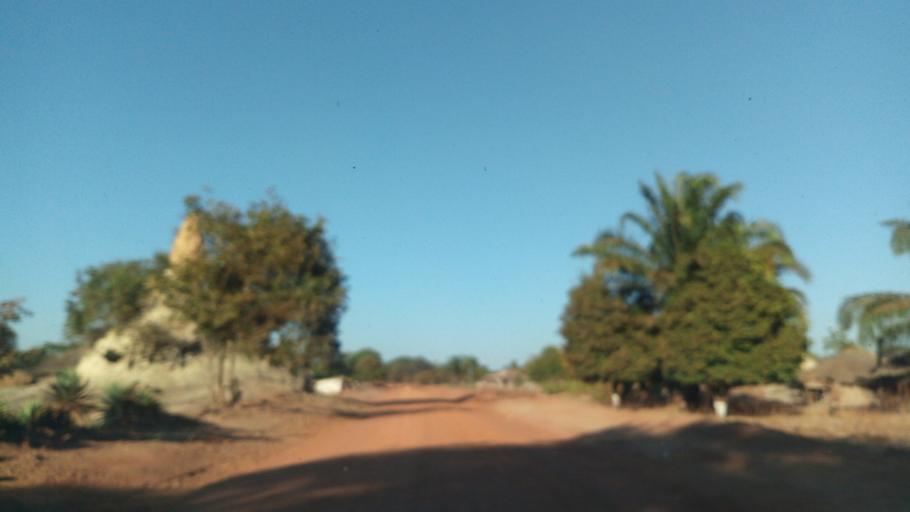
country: ZM
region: Luapula
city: Mwense
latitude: -10.4692
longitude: 28.5176
